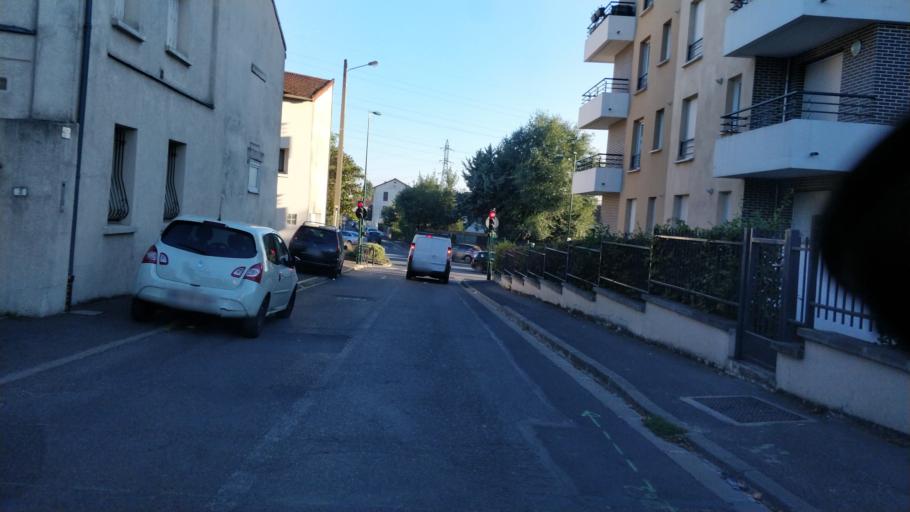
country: FR
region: Ile-de-France
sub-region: Departement de Seine-Saint-Denis
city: Gagny
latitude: 48.8823
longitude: 2.5391
